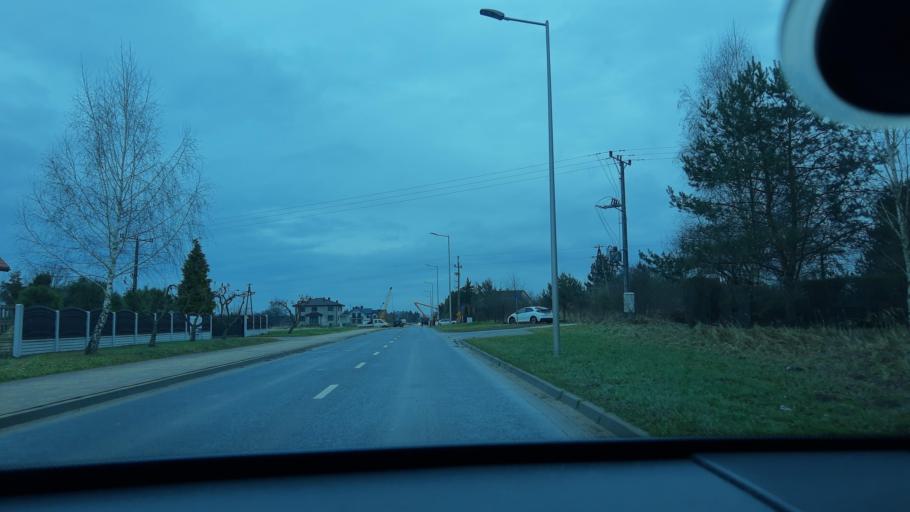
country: PL
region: Lodz Voivodeship
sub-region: Powiat sieradzki
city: Sieradz
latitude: 51.5881
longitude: 18.6937
